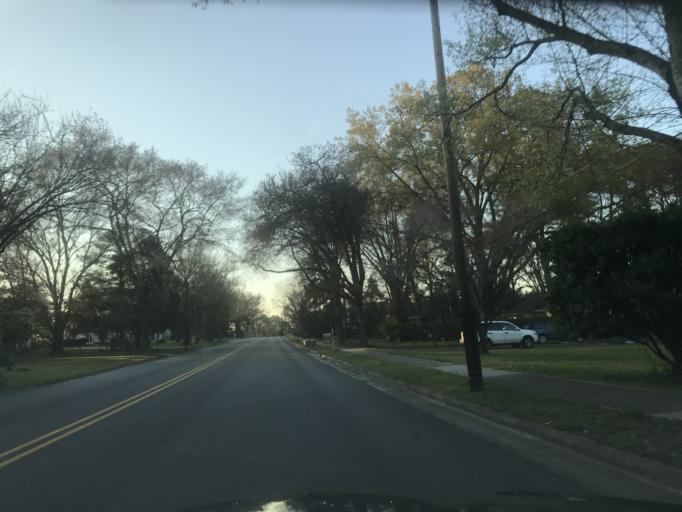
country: US
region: North Carolina
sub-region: Wake County
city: Raleigh
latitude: 35.7771
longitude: -78.6061
